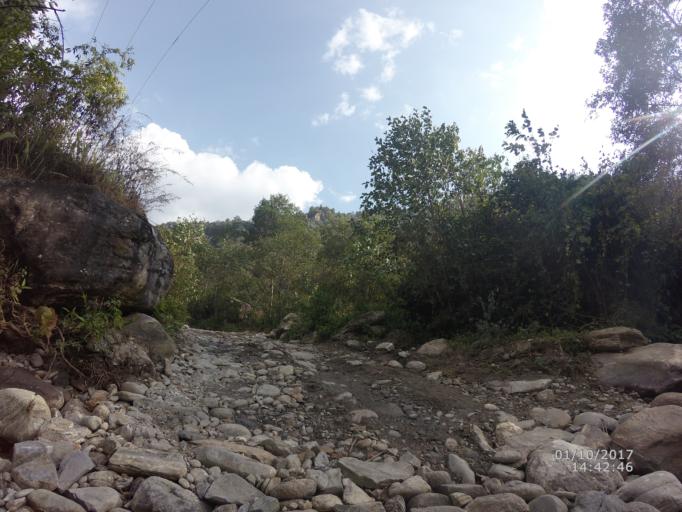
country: NP
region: Western Region
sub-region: Gandaki Zone
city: Pokhara
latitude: 28.3451
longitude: 83.9762
